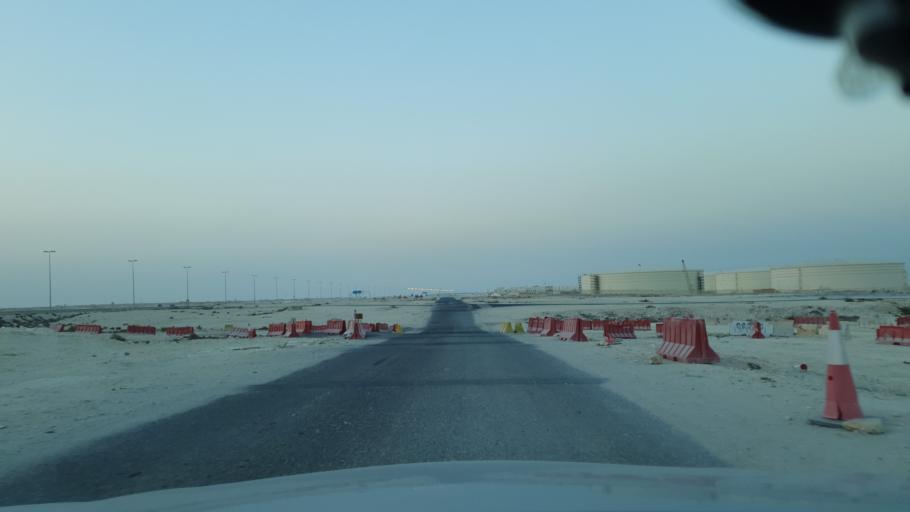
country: BH
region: Central Governorate
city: Dar Kulayb
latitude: 25.9731
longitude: 50.6021
